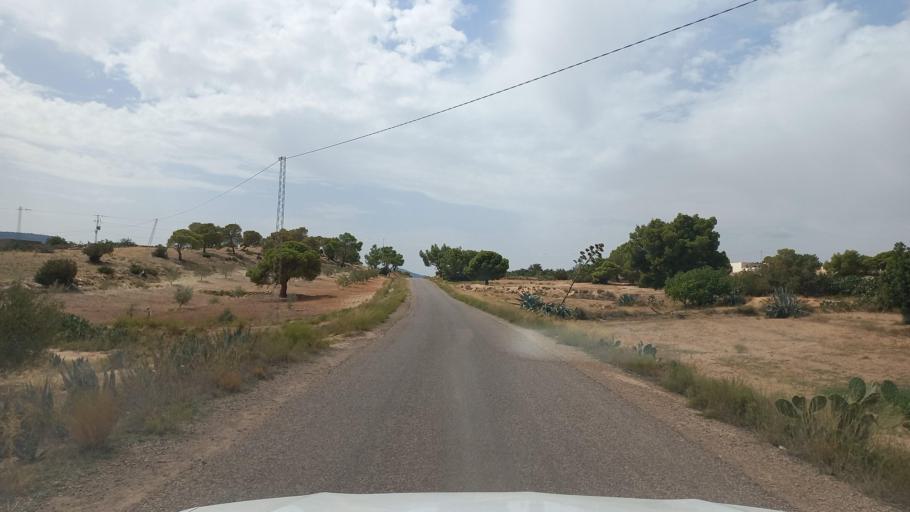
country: TN
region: Al Qasrayn
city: Kasserine
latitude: 35.3732
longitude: 8.8989
